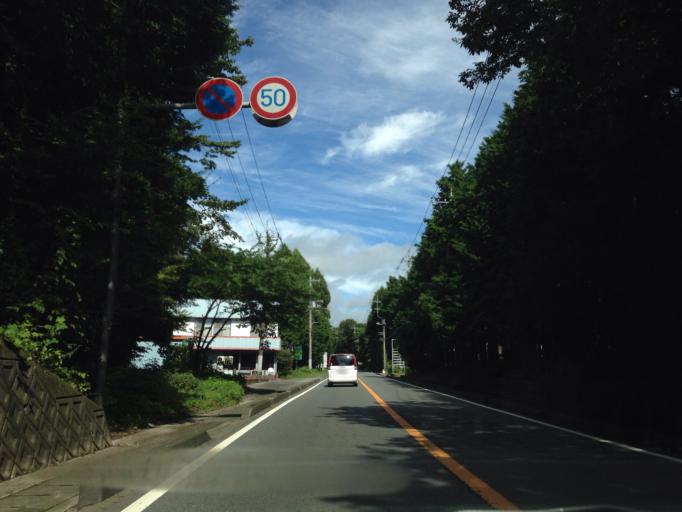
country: JP
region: Shizuoka
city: Gotemba
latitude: 35.3319
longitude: 138.9014
